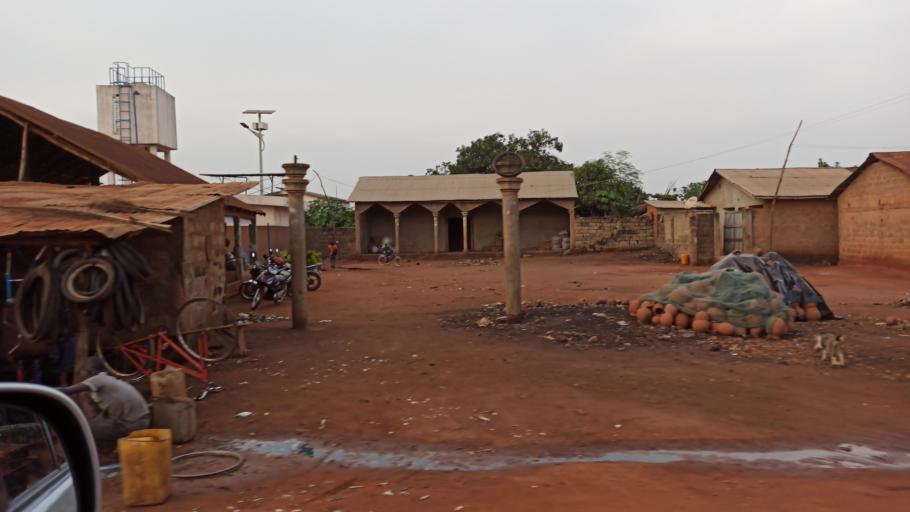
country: BJ
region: Queme
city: Porto-Novo
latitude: 6.5325
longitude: 2.6626
